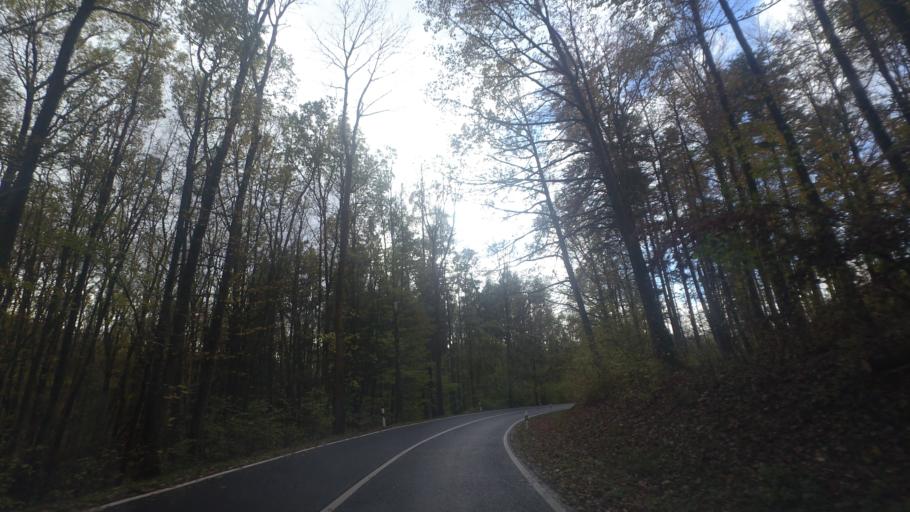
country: DE
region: Thuringia
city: Dingsleben
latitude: 50.4100
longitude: 10.6149
